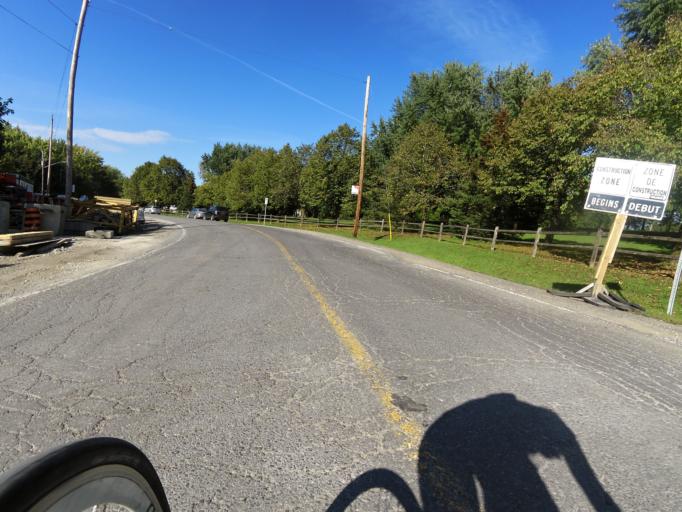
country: CA
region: Ontario
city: Bells Corners
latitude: 45.2443
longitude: -75.7017
